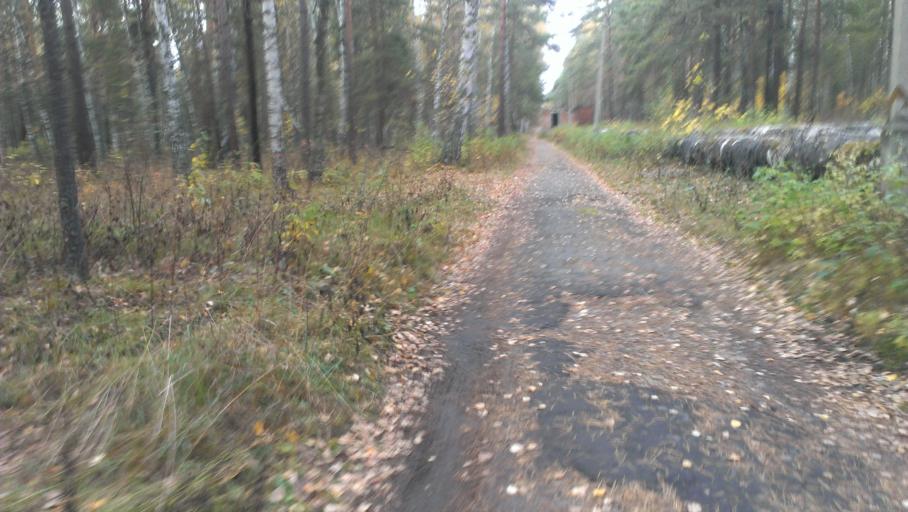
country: RU
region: Altai Krai
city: Yuzhnyy
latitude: 53.2684
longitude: 83.6822
